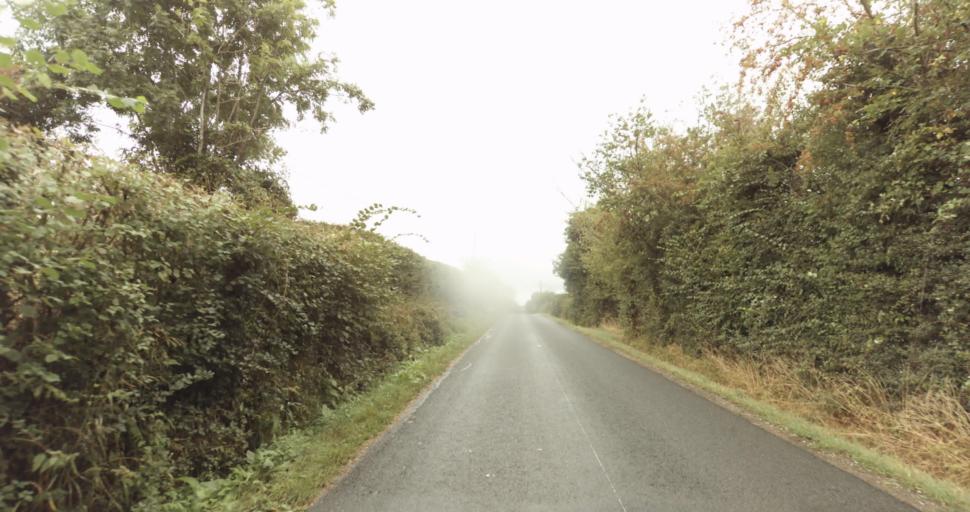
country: FR
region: Lower Normandy
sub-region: Departement de l'Orne
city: Vimoutiers
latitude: 48.8929
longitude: 0.2114
